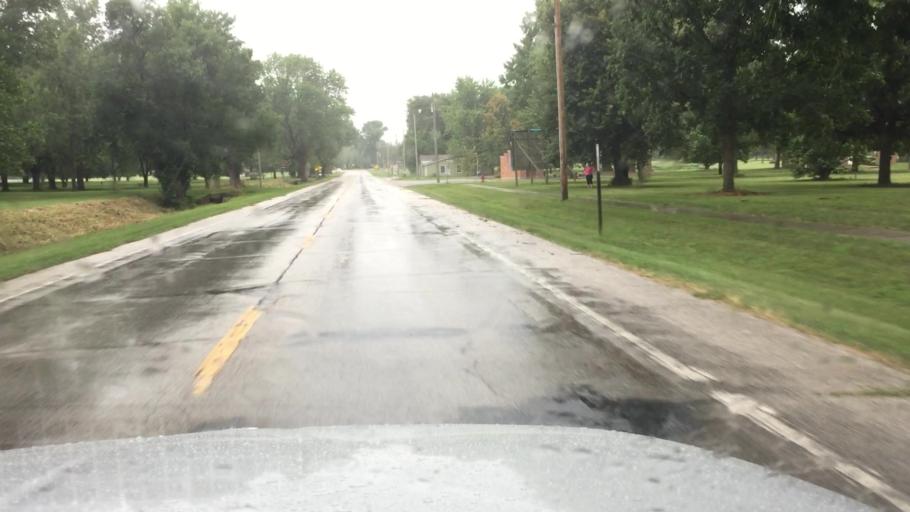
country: US
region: Illinois
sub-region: Hancock County
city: Nauvoo
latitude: 40.5450
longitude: -91.3866
